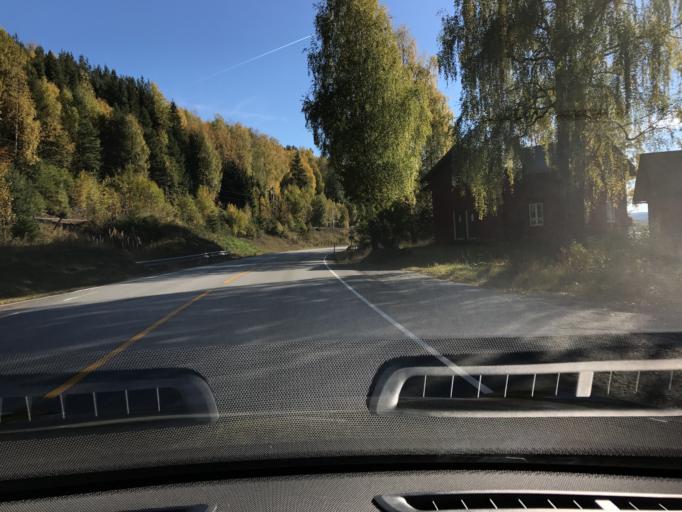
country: NO
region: Buskerud
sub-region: Fla
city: Fla
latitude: 60.3708
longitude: 9.6374
